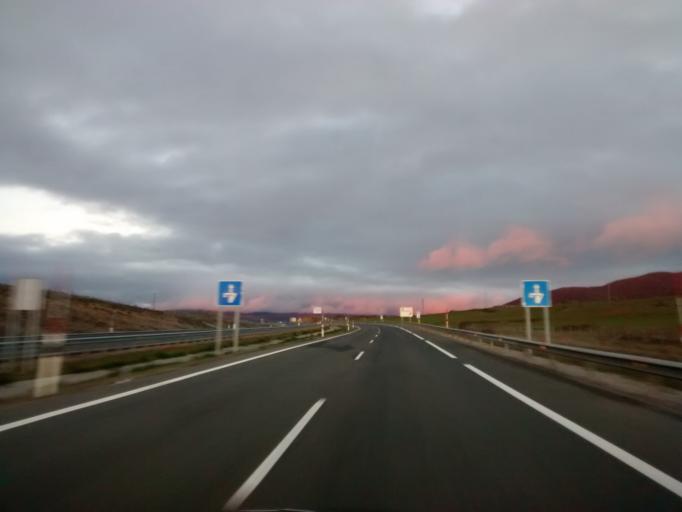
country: ES
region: Cantabria
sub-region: Provincia de Cantabria
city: Mataporquera
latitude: 42.8601
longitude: -4.1600
